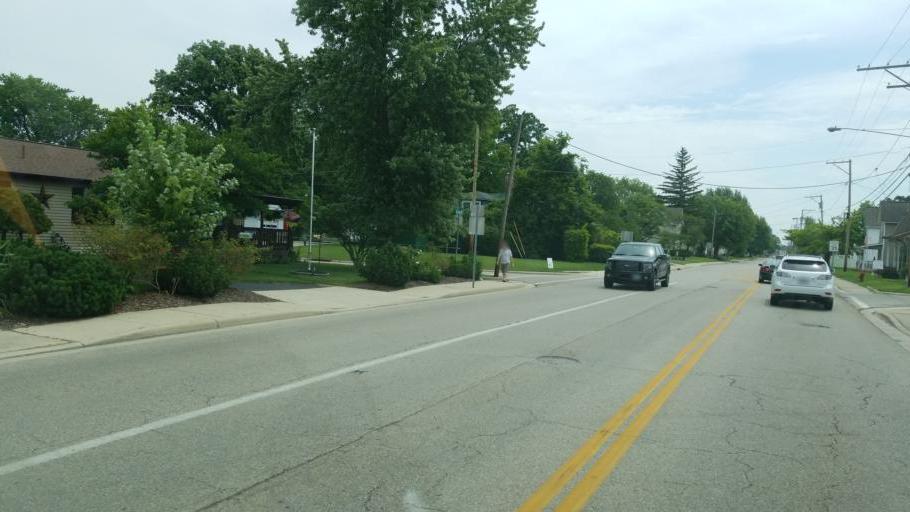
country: US
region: Ohio
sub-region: Madison County
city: Plain City
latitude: 40.1104
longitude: -83.2771
